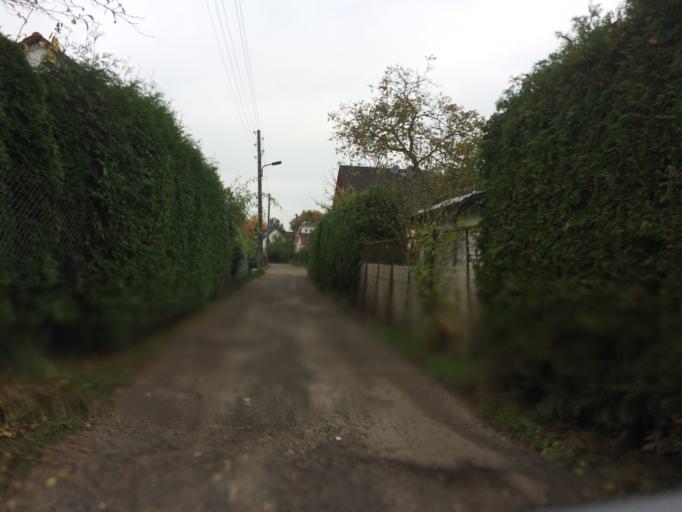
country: DE
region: Berlin
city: Wilhelmsruh
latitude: 52.5789
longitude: 13.3717
